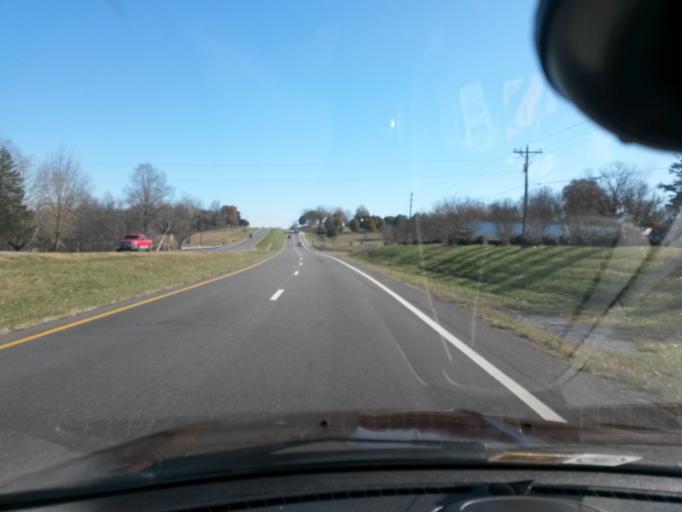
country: US
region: Virginia
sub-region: Bedford County
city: Forest
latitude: 37.3008
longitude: -79.3763
